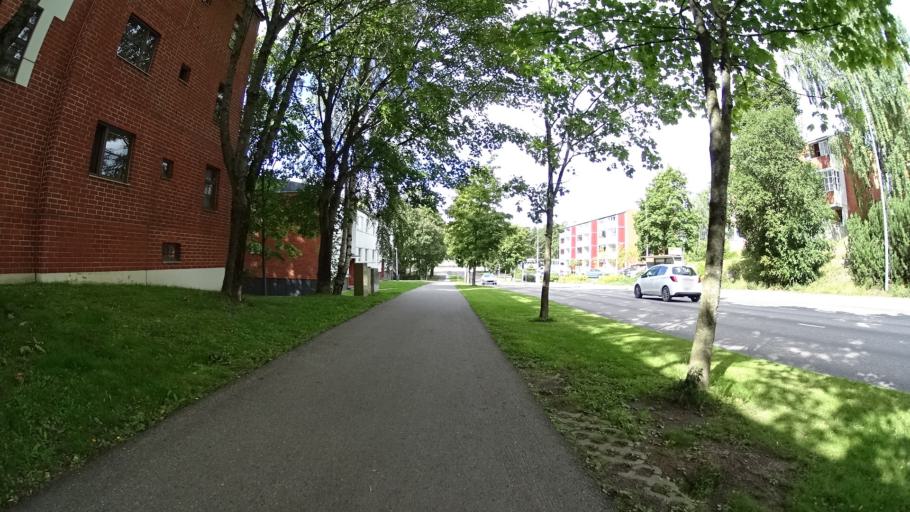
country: FI
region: Uusimaa
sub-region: Helsinki
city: Kilo
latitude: 60.2277
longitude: 24.8199
